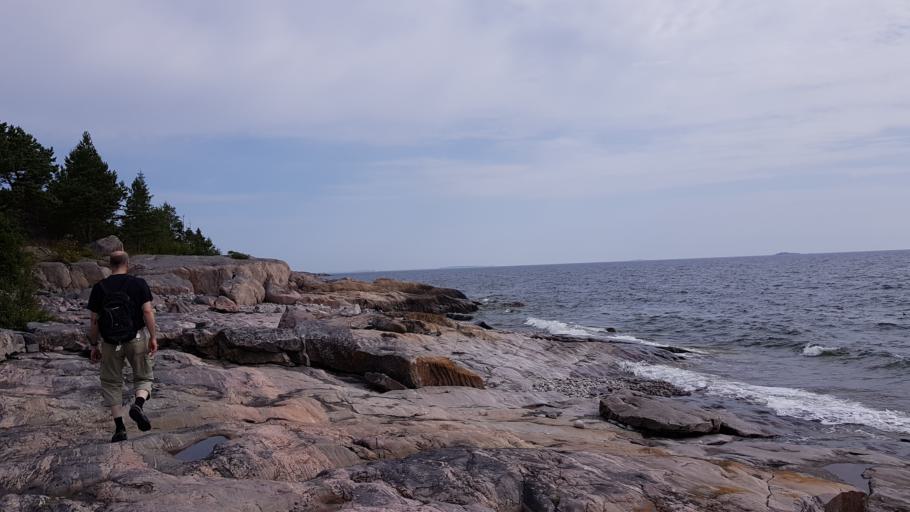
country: FI
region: Uusimaa
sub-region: Helsinki
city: Helsinki
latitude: 60.0966
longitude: 25.0487
